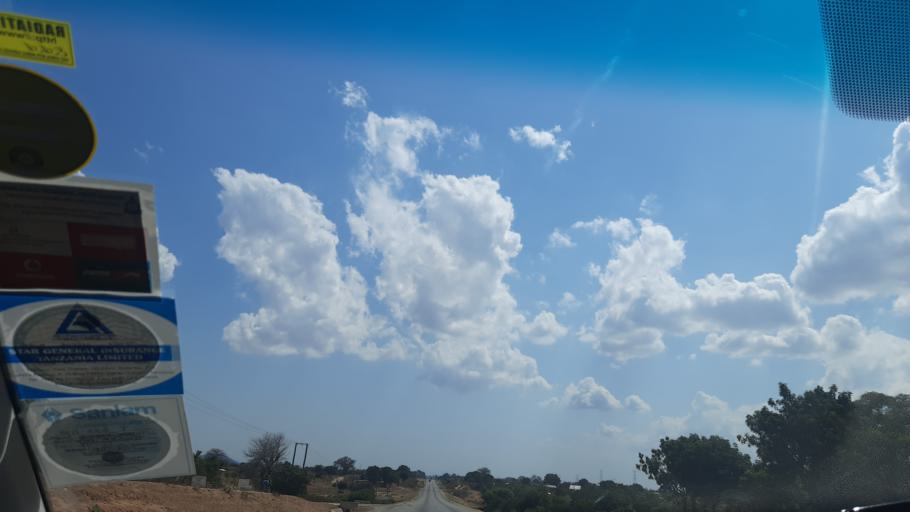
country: TZ
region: Singida
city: Kintinku
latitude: -6.0120
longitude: 35.4271
